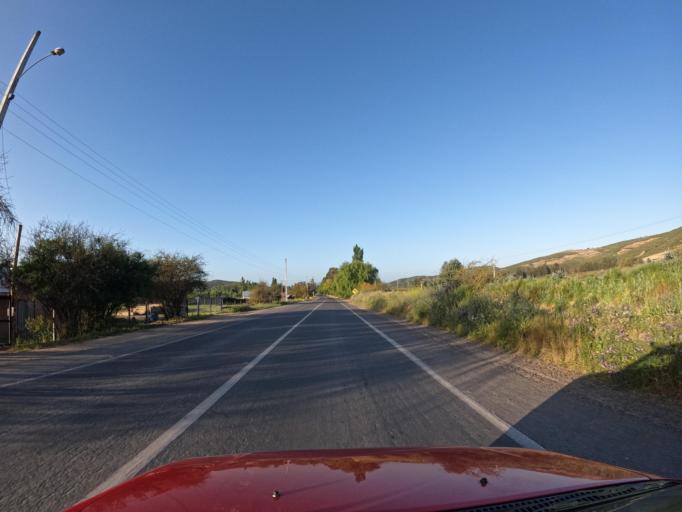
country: CL
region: O'Higgins
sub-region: Provincia de Colchagua
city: Santa Cruz
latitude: -34.3353
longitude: -71.3985
